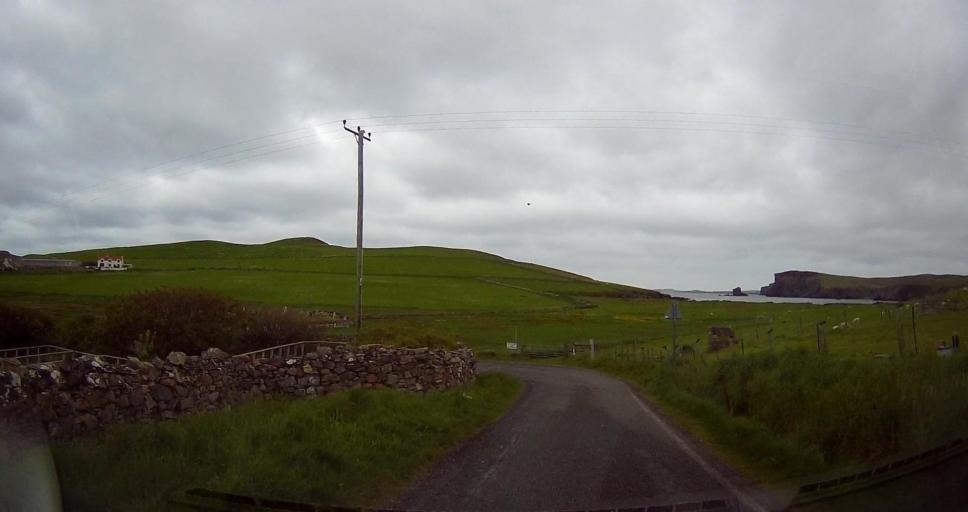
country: GB
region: Scotland
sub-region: Shetland Islands
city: Lerwick
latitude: 60.4764
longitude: -1.4889
